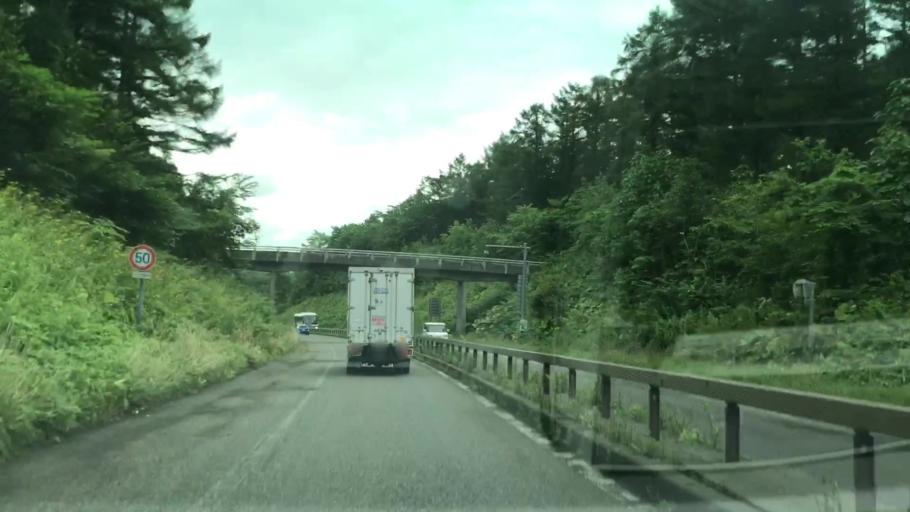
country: JP
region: Hokkaido
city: Chitose
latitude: 42.8107
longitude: 141.6274
